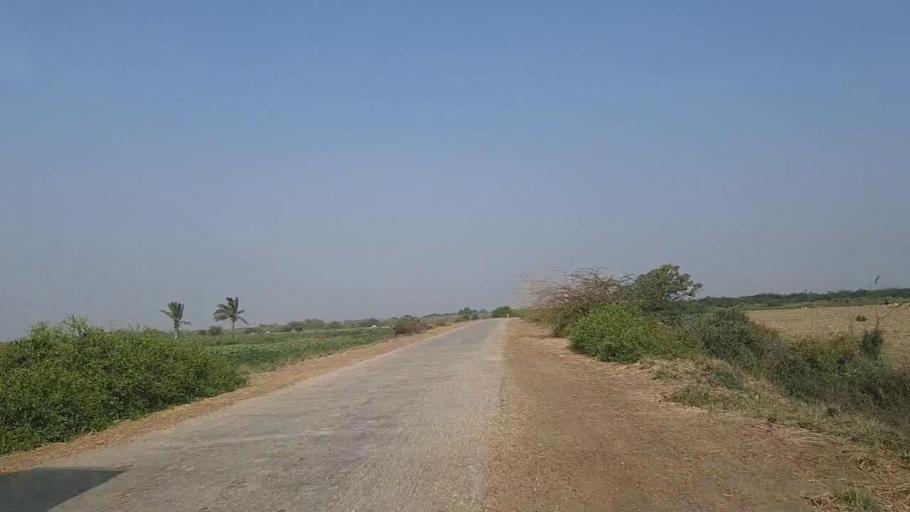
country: PK
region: Sindh
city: Keti Bandar
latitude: 24.2443
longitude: 67.7087
